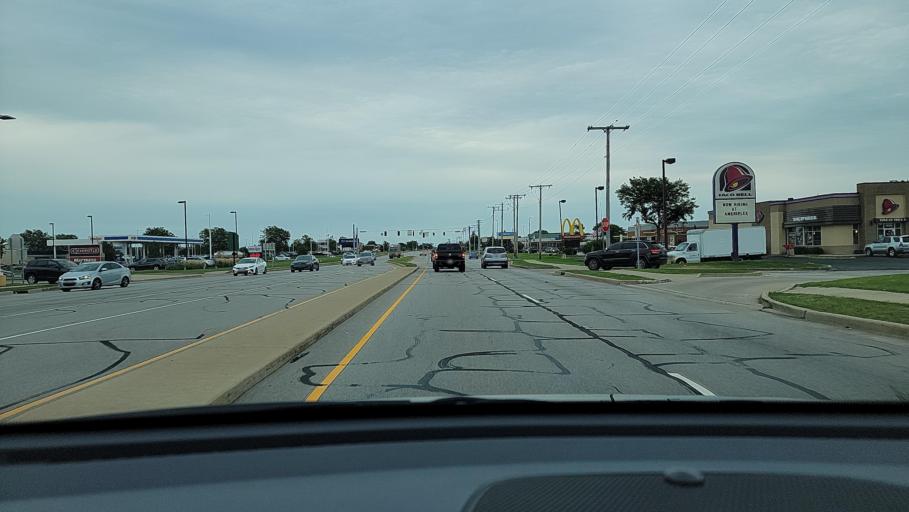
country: US
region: Indiana
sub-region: Porter County
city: Portage
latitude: 41.5504
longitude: -87.1817
